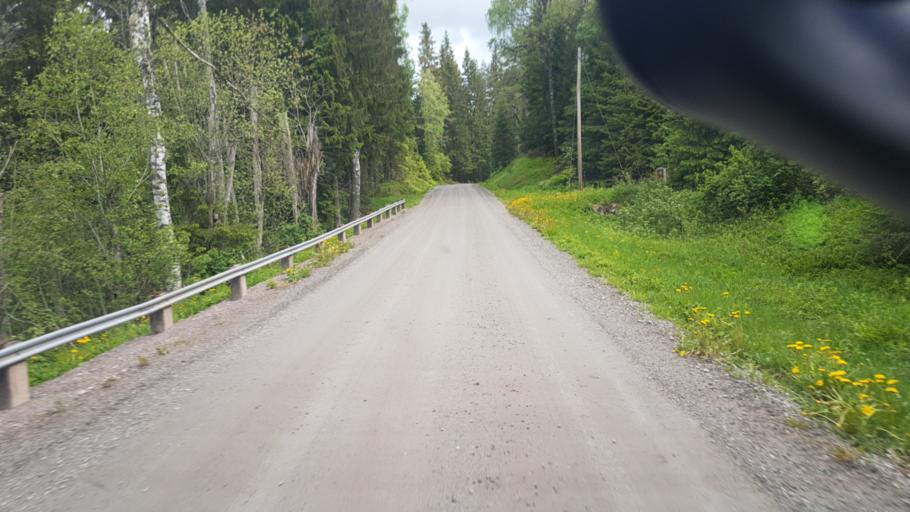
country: NO
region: Ostfold
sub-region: Romskog
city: Romskog
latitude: 59.7106
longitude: 11.9697
